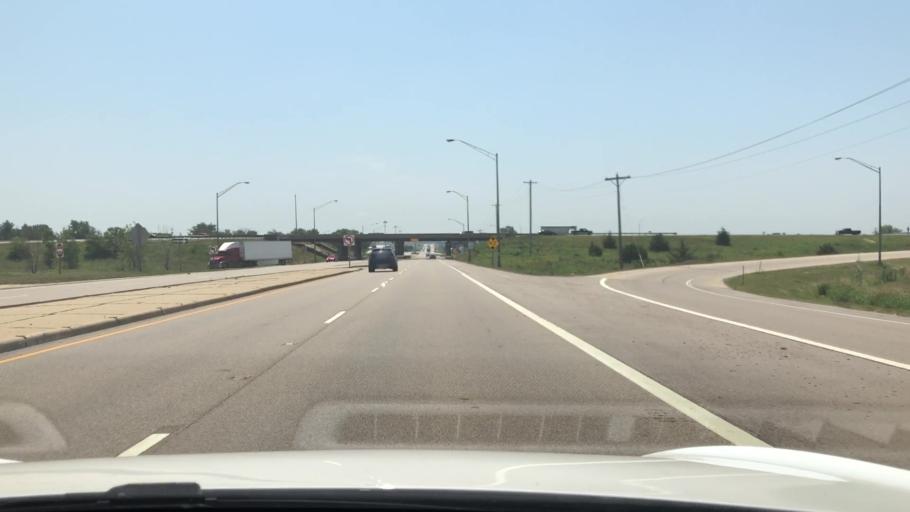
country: US
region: Illinois
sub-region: McLean County
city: Bloomington
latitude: 40.4380
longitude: -88.9907
